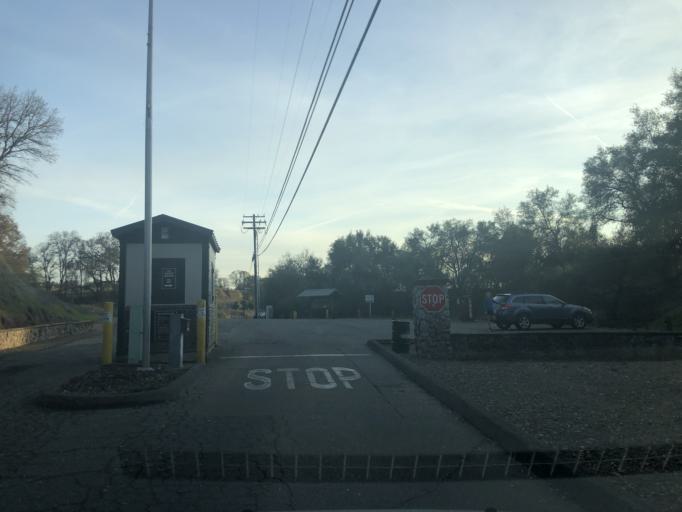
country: US
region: California
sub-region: Sacramento County
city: Gold River
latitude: 38.6422
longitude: -121.2347
